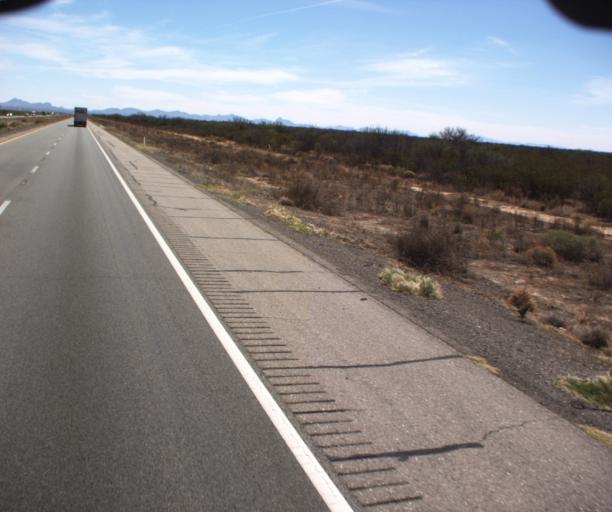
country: US
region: Arizona
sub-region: Cochise County
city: Willcox
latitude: 32.2904
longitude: -109.3244
